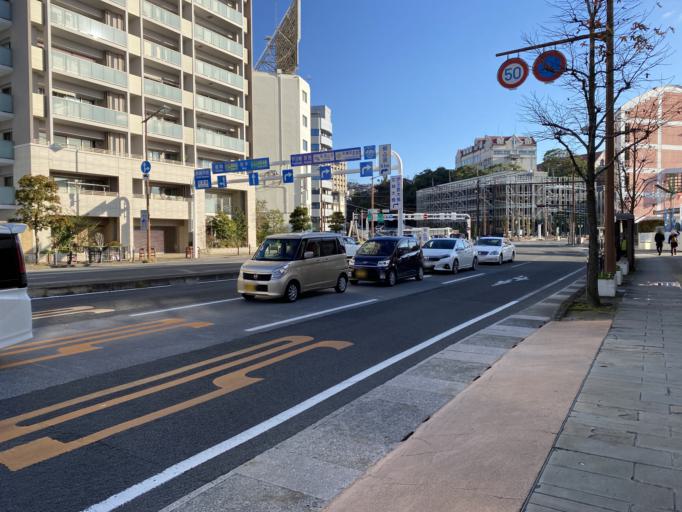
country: JP
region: Nagasaki
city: Nagasaki-shi
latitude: 32.7417
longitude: 129.8723
